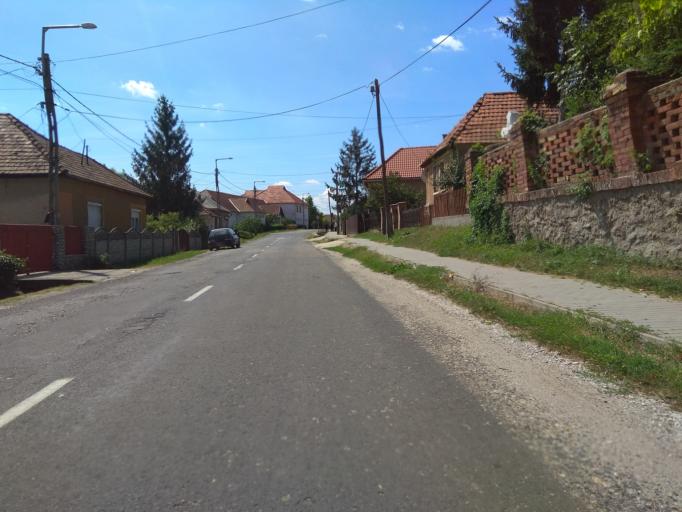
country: HU
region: Borsod-Abauj-Zemplen
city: Izsofalva
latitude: 48.2817
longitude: 20.6514
